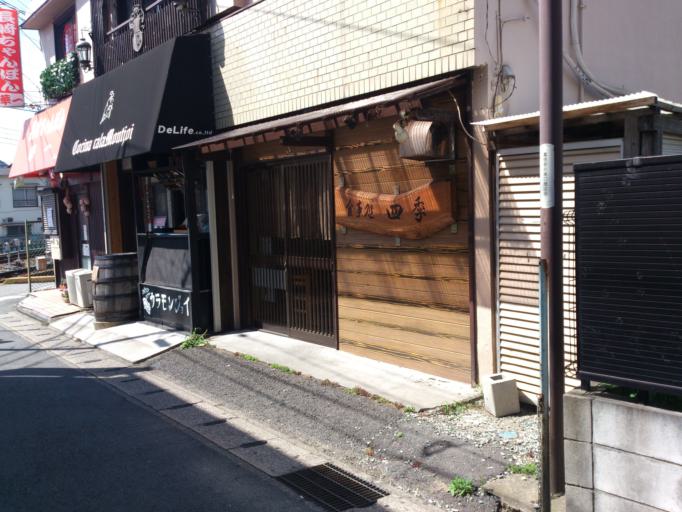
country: JP
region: Chiba
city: Funabashi
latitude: 35.6593
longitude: 140.0566
